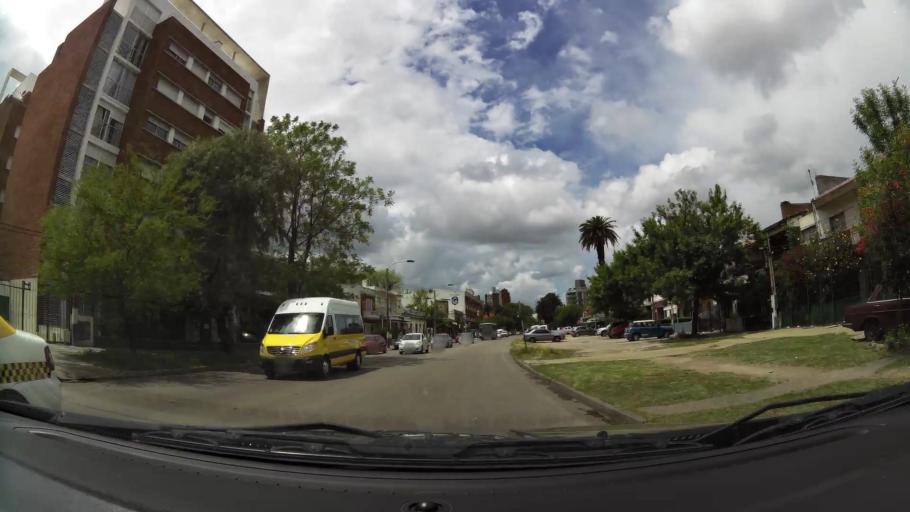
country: UY
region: Montevideo
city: Montevideo
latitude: -34.8742
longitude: -56.1592
